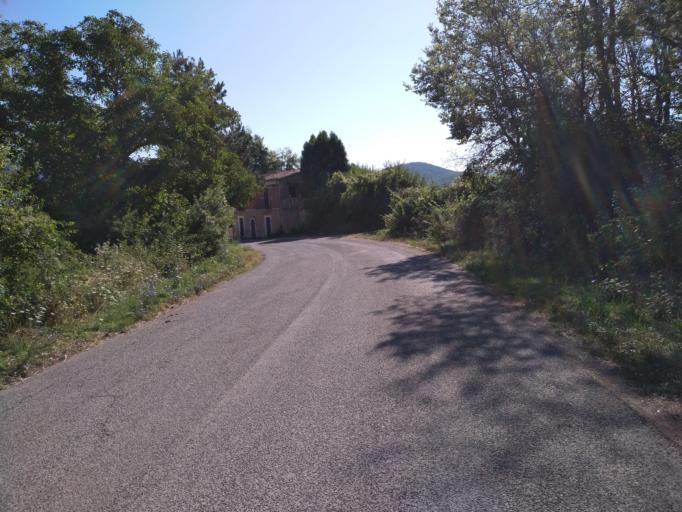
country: IT
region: Abruzzo
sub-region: Provincia dell' Aquila
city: Secinaro
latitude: 42.1798
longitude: 13.6671
